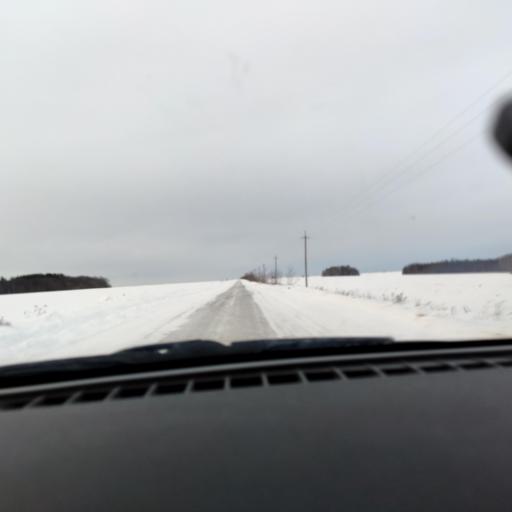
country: RU
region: Bashkortostan
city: Iglino
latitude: 54.7424
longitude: 56.5356
